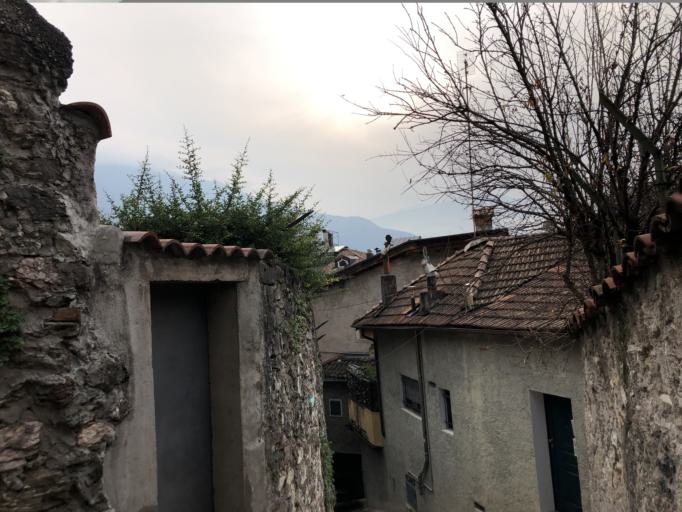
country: IT
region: Trentino-Alto Adige
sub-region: Provincia di Trento
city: Arco
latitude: 45.9201
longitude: 10.8861
